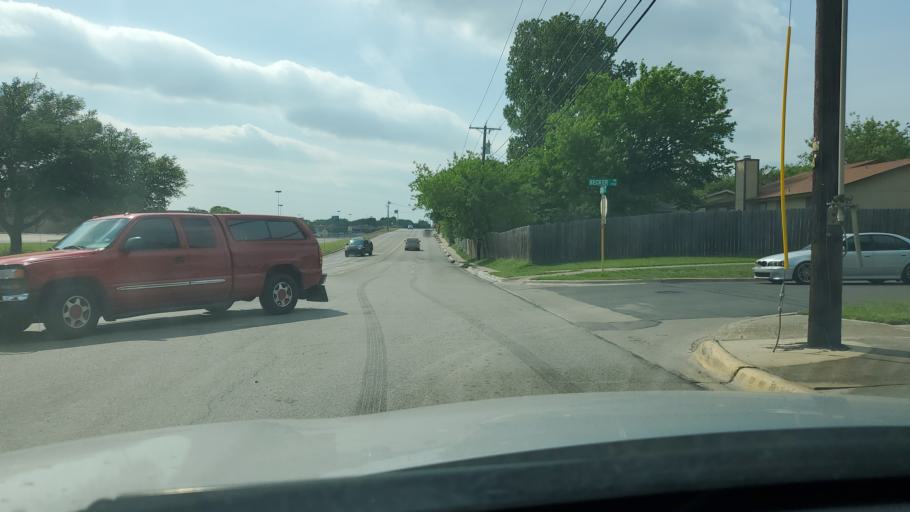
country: US
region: Texas
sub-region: Bell County
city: Killeen
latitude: 31.0938
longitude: -97.7139
